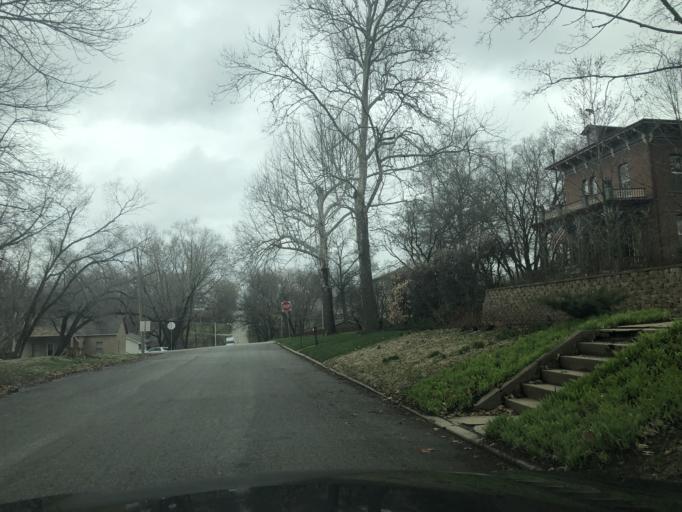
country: US
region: Kansas
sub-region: Leavenworth County
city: Leavenworth
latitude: 39.3069
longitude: -94.9149
